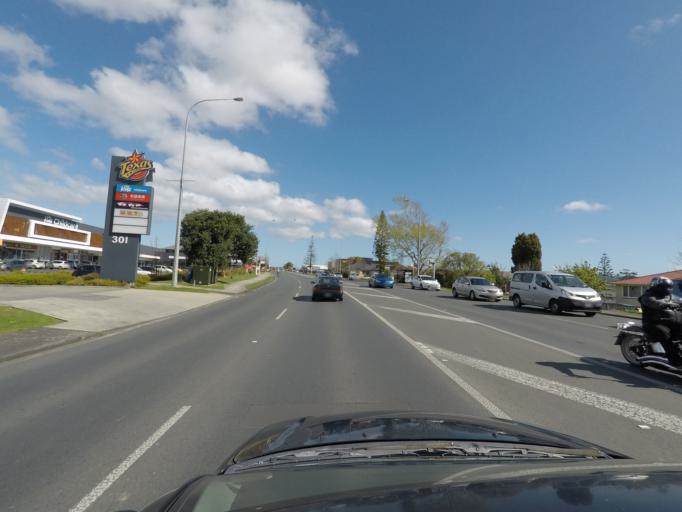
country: NZ
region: Auckland
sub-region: Auckland
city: Rosebank
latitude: -36.8523
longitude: 174.6302
